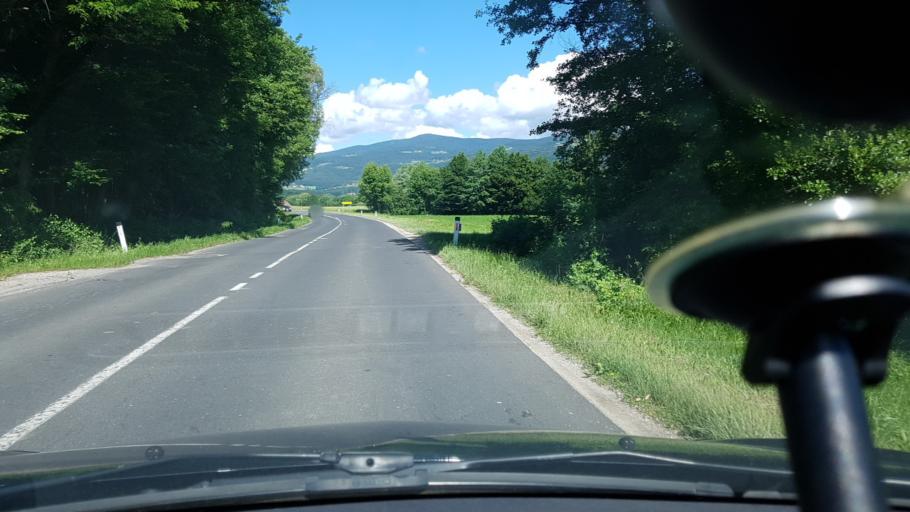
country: SI
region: Slovenska Bistrica
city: Slovenska Bistrica
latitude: 46.3760
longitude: 15.5453
